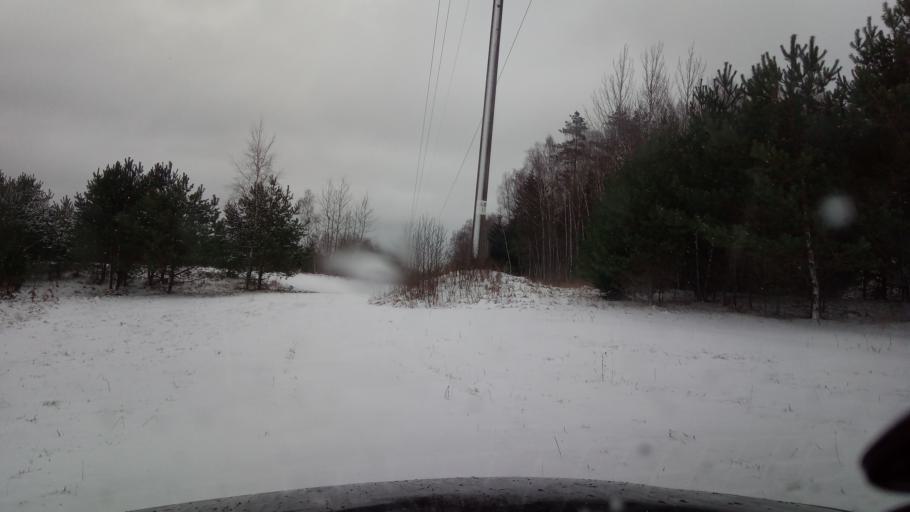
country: LT
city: Zarasai
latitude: 55.6404
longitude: 25.9815
